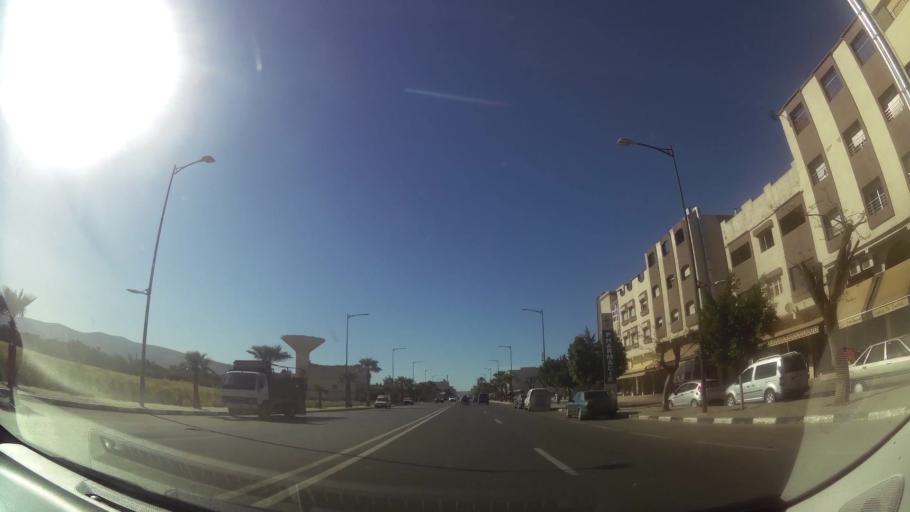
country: MA
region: Oriental
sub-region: Berkane-Taourirt
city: Ahfir
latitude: 34.8562
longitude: -1.9918
